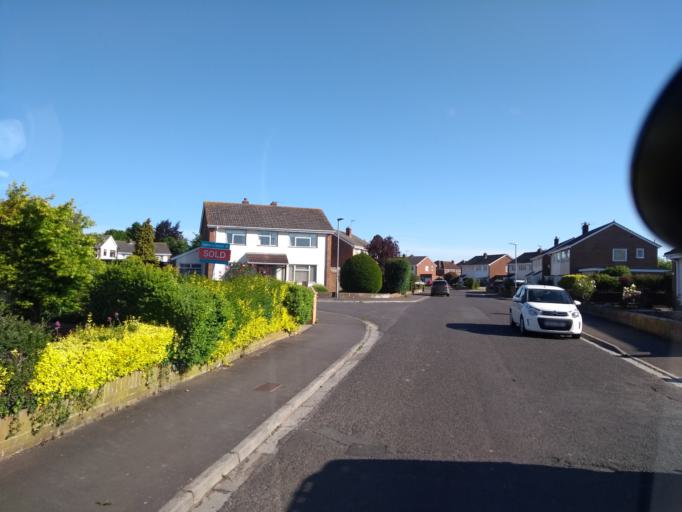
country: GB
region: England
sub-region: Somerset
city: North Petherton
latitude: 51.0931
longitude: -3.0080
